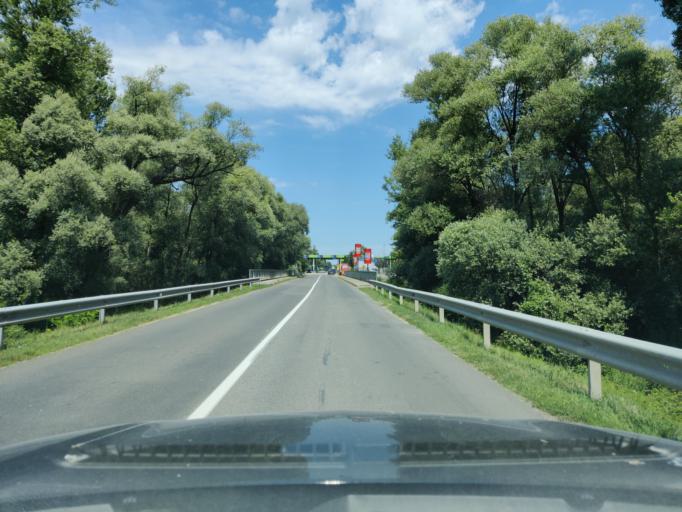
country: HR
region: Medimurska
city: Peklenica
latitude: 46.5164
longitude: 16.4410
